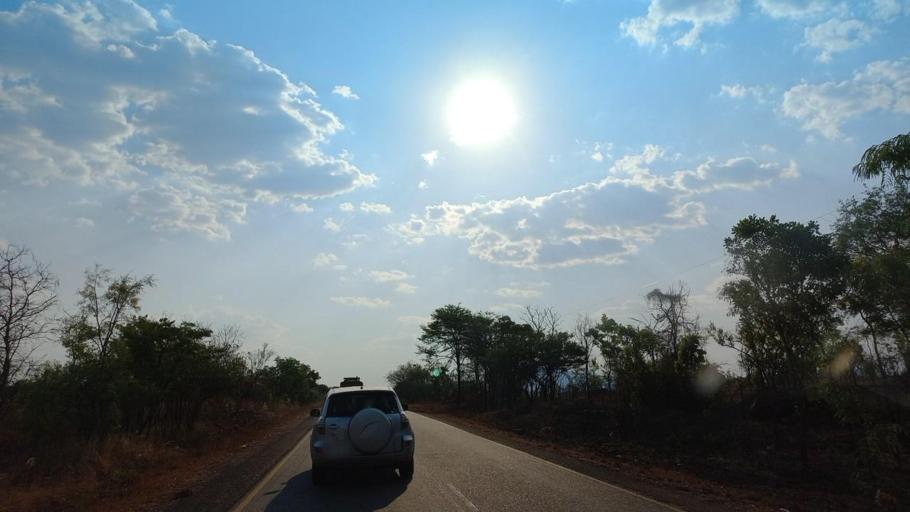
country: ZM
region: Lusaka
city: Luangwa
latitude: -14.9774
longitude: 29.9960
